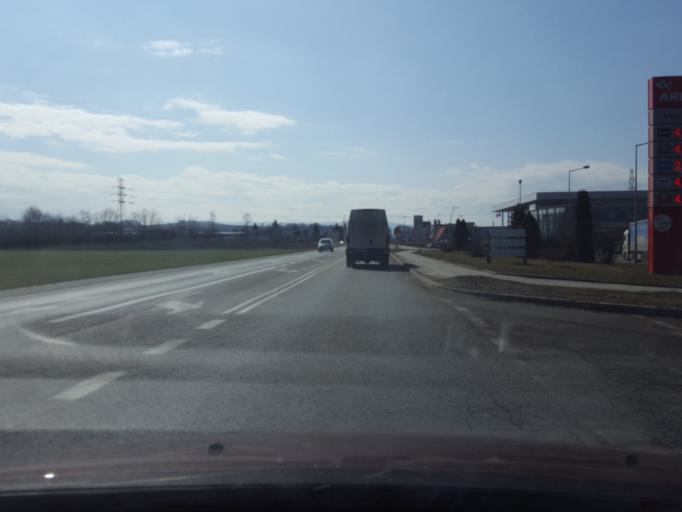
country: PL
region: Lesser Poland Voivodeship
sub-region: Powiat nowosadecki
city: Chelmiec
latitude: 49.6597
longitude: 20.6893
